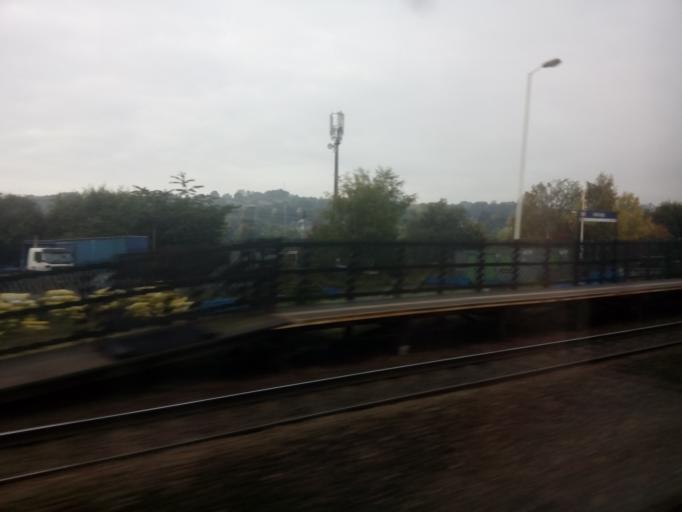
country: GB
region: England
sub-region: Kirklees
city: Mirfield
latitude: 53.6711
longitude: -1.6902
